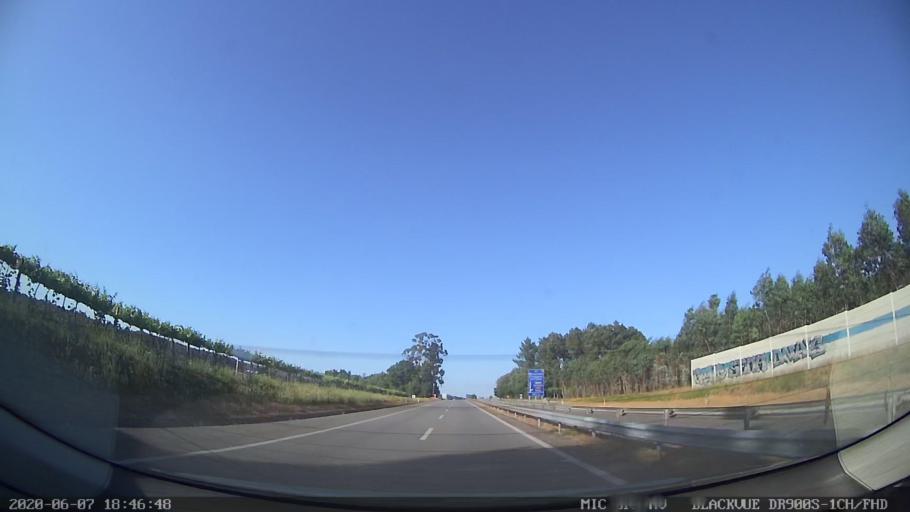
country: PT
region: Braga
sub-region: Vila Nova de Famalicao
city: Vila Nova de Famalicao
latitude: 41.3973
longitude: -8.4695
